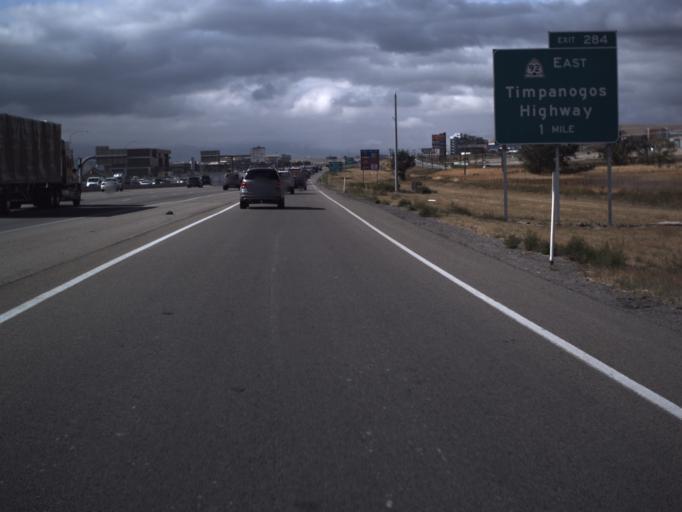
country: US
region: Utah
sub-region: Utah County
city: Lehi
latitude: 40.4163
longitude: -111.8729
